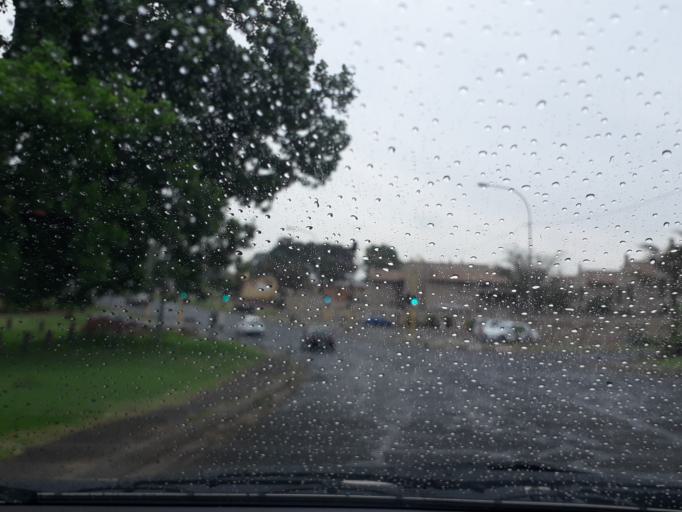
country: ZA
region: Gauteng
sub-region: City of Johannesburg Metropolitan Municipality
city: Modderfontein
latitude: -26.1457
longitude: 28.1046
